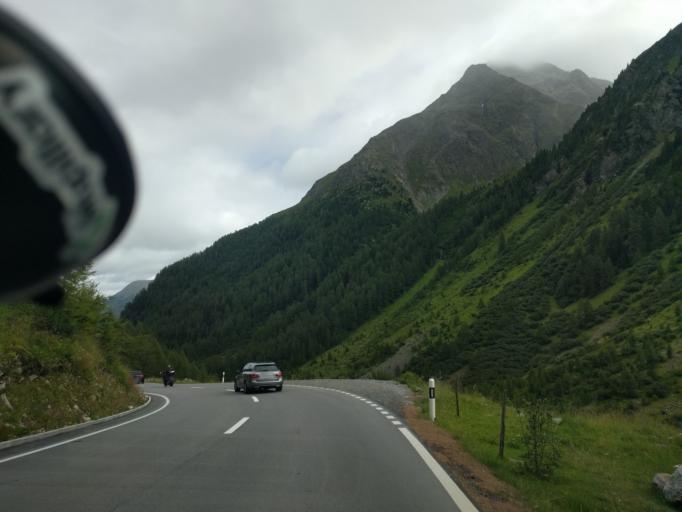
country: CH
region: Grisons
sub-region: Inn District
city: Zernez
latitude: 46.7513
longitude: 10.0106
